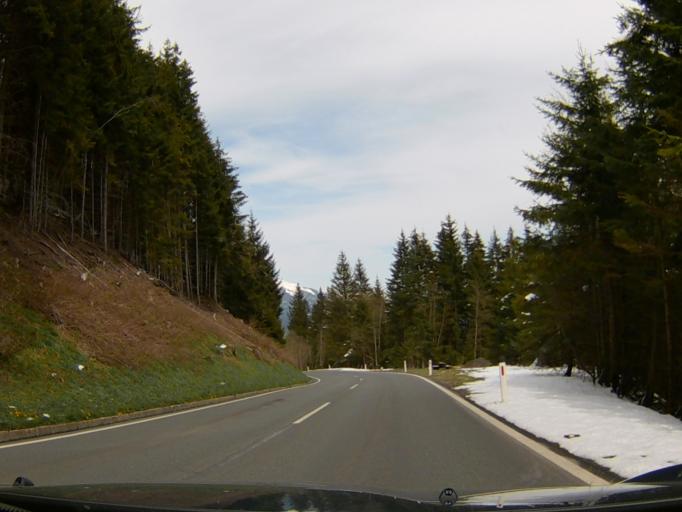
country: AT
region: Salzburg
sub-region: Politischer Bezirk Zell am See
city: Krimml
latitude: 47.2195
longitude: 12.1542
